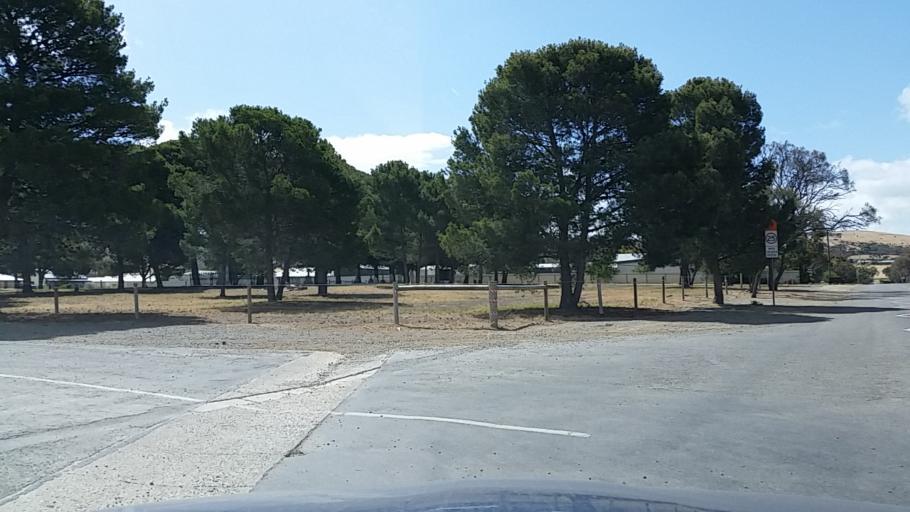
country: AU
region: South Australia
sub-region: Alexandrina
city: Port Elliot
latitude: -35.5244
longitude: 138.6770
